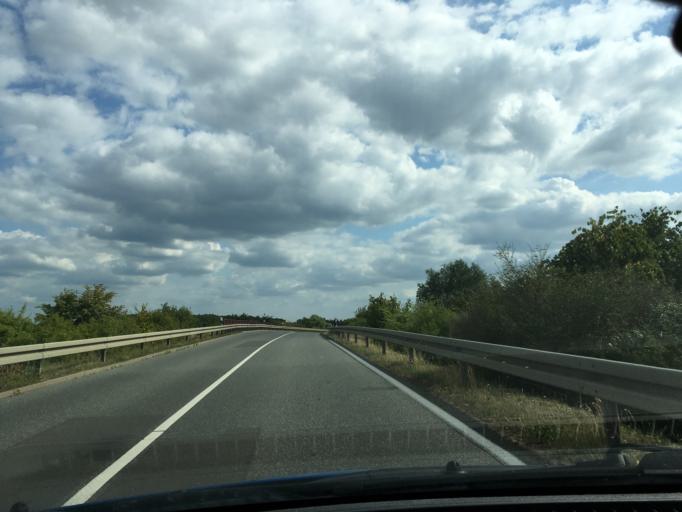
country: DE
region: Mecklenburg-Vorpommern
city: Lubtheen
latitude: 53.3660
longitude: 11.0855
